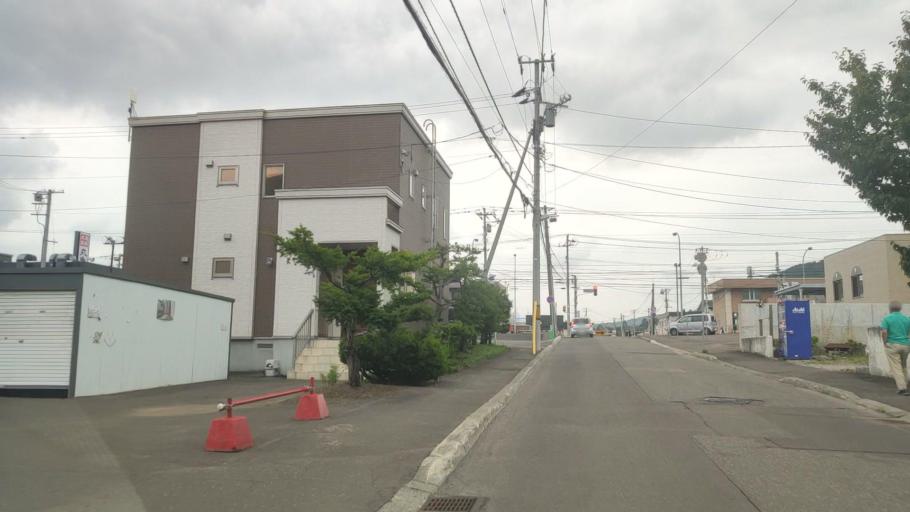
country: JP
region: Hokkaido
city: Sapporo
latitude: 42.9625
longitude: 141.3187
